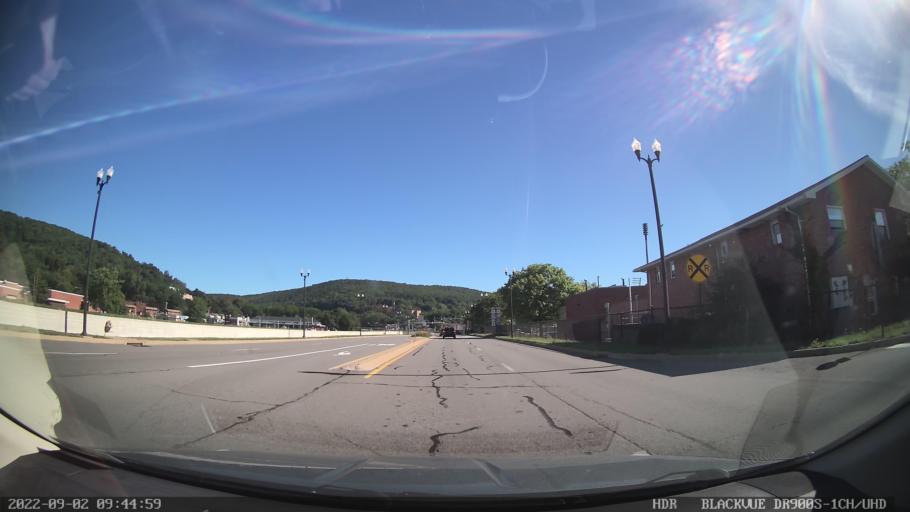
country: US
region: Pennsylvania
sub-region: Montour County
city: Danville
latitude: 40.9627
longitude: -76.6187
